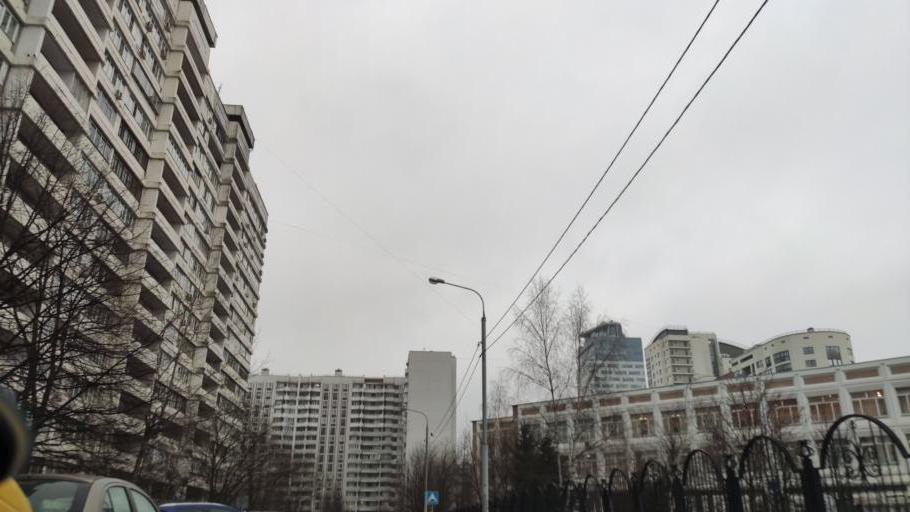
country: RU
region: Moskovskaya
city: Bol'shaya Setun'
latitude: 55.7446
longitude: 37.4294
